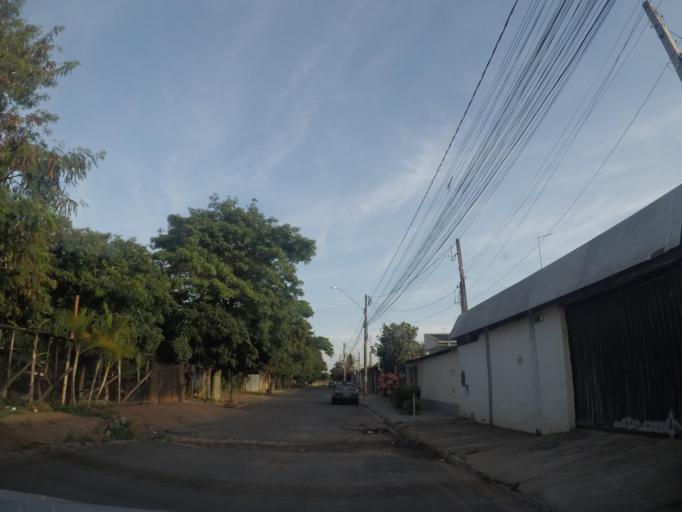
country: BR
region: Sao Paulo
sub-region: Hortolandia
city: Hortolandia
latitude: -22.8463
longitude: -47.1846
